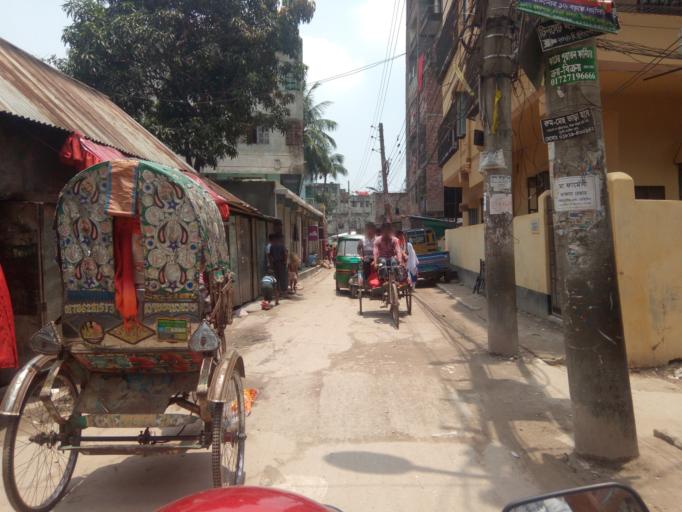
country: BD
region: Dhaka
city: Paltan
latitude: 23.7580
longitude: 90.4323
